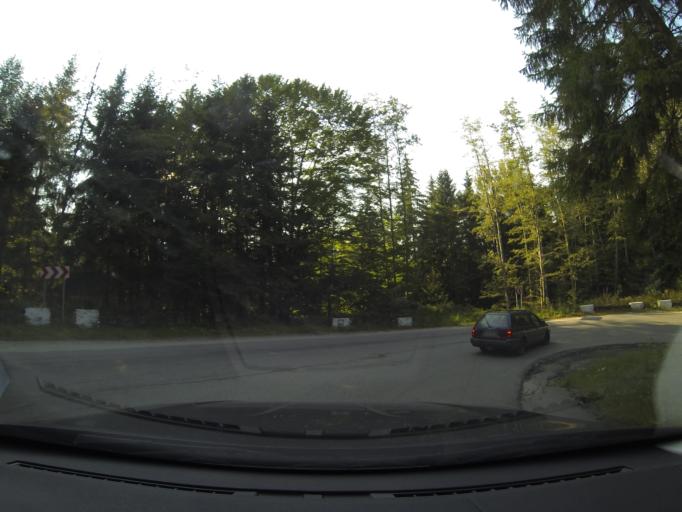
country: RO
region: Arges
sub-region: Comuna Arefu
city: Arefu
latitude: 45.4072
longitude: 24.6337
